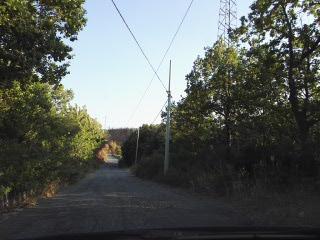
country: IT
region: Calabria
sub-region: Provincia di Reggio Calabria
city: Caulonia
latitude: 38.4118
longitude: 16.3608
